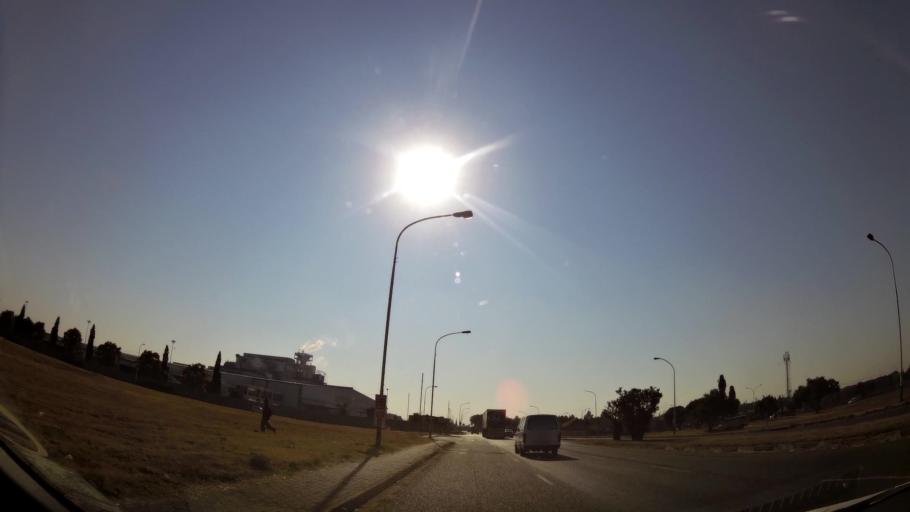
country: ZA
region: Gauteng
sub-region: Ekurhuleni Metropolitan Municipality
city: Boksburg
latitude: -26.2232
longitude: 28.2698
